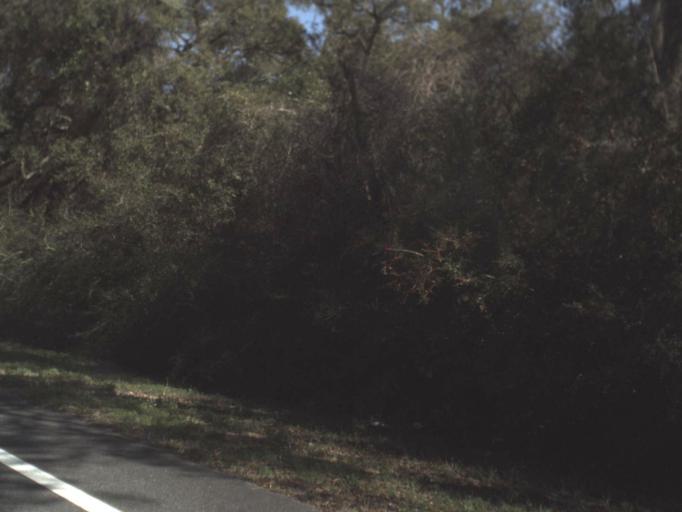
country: US
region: Florida
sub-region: Franklin County
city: Carrabelle
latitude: 29.9324
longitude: -84.4538
